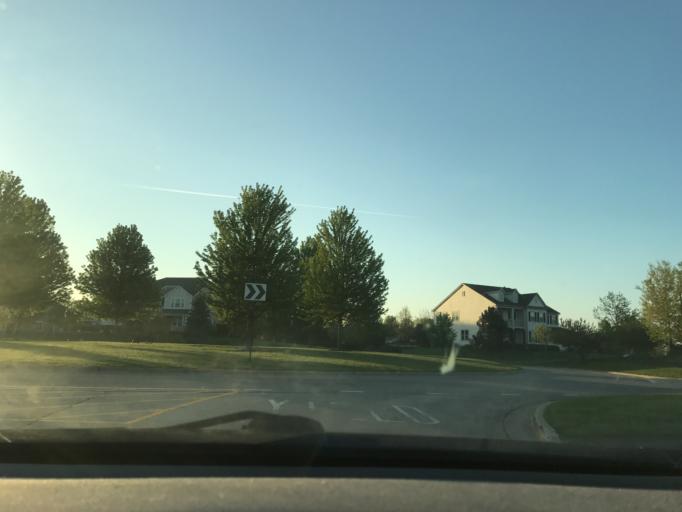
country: US
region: Illinois
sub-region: Kane County
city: Pingree Grove
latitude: 42.0276
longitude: -88.3621
